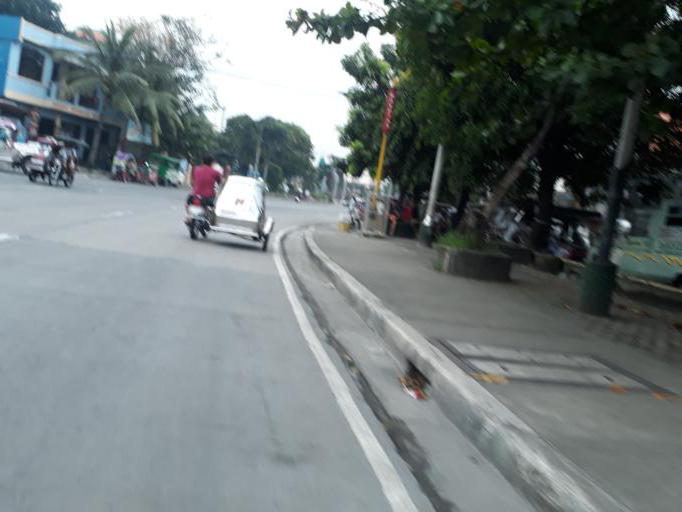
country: PH
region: Metro Manila
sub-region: Caloocan City
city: Niugan
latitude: 14.6521
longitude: 120.9487
